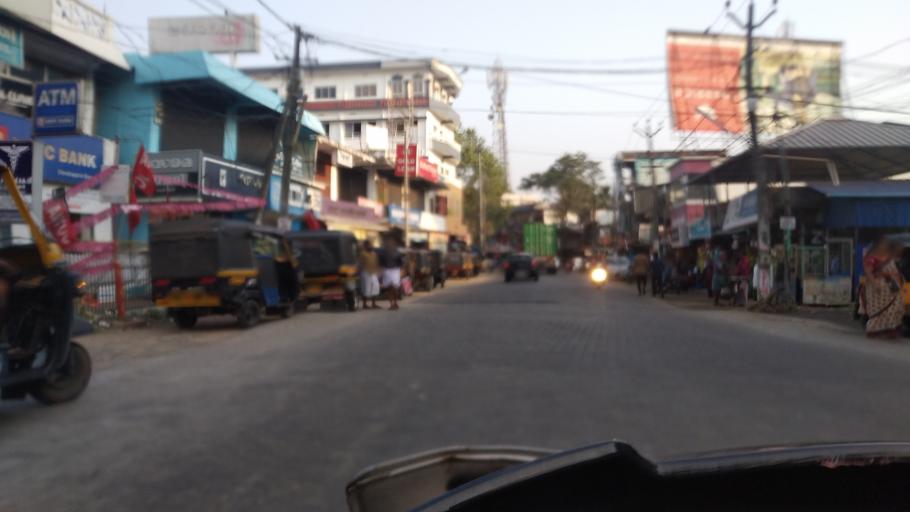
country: IN
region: Kerala
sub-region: Thrissur District
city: Thanniyam
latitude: 10.3562
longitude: 76.1281
